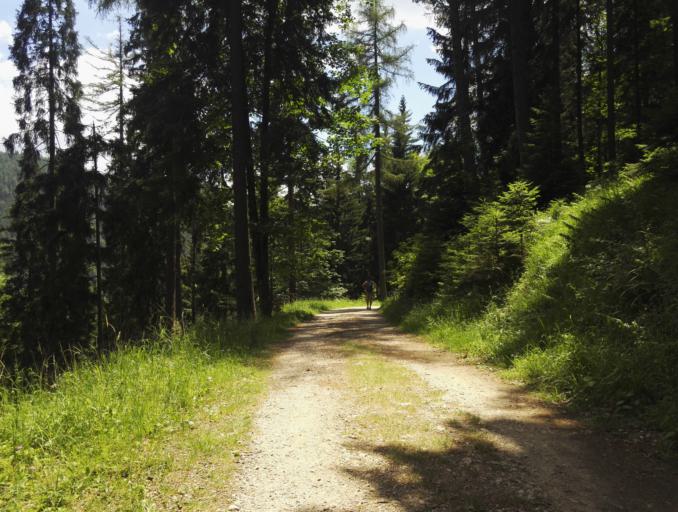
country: AT
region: Styria
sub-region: Politischer Bezirk Graz-Umgebung
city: Rothelstein
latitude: 47.3507
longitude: 15.4041
